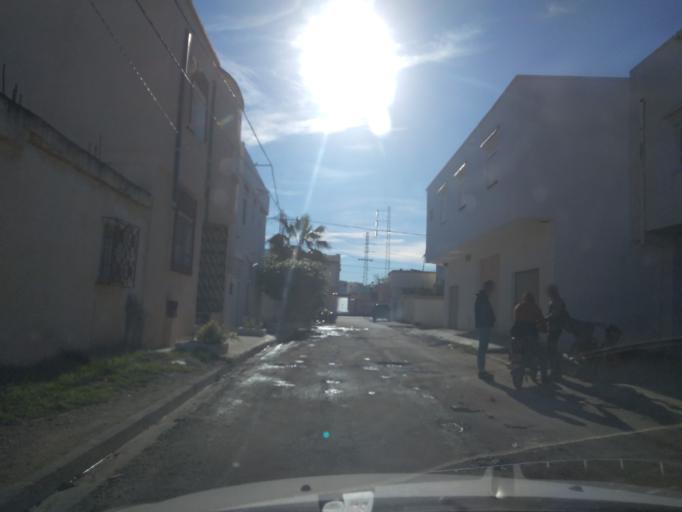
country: TN
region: Ariana
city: Qal'at al Andalus
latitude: 37.0620
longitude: 10.1242
